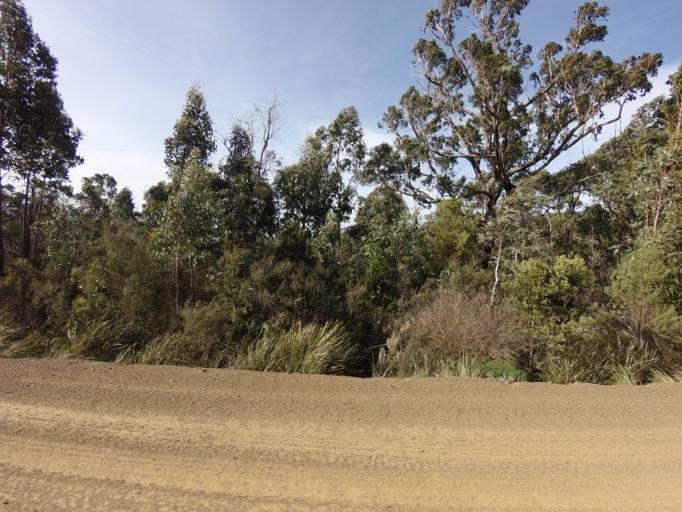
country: AU
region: Tasmania
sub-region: Kingborough
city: Kettering
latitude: -43.0826
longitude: 147.2648
